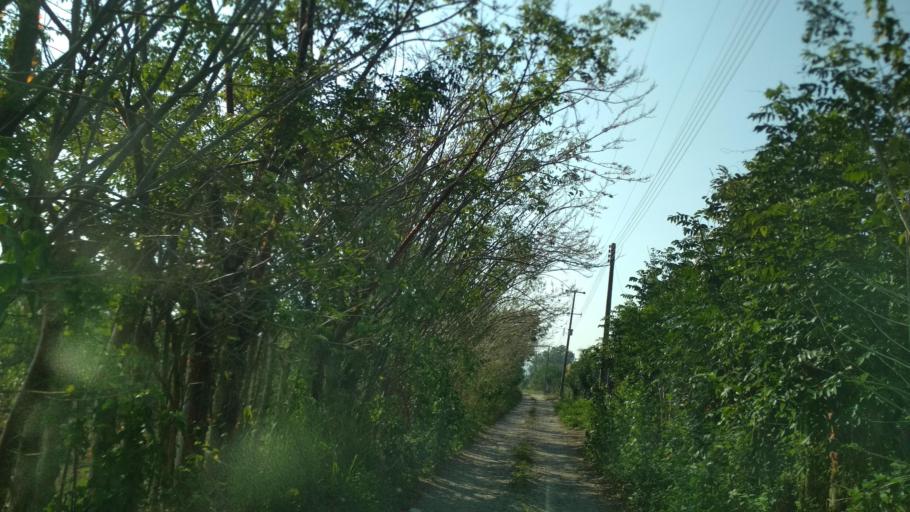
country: MX
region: Veracruz
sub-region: Papantla
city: Polutla
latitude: 20.4610
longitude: -97.2085
